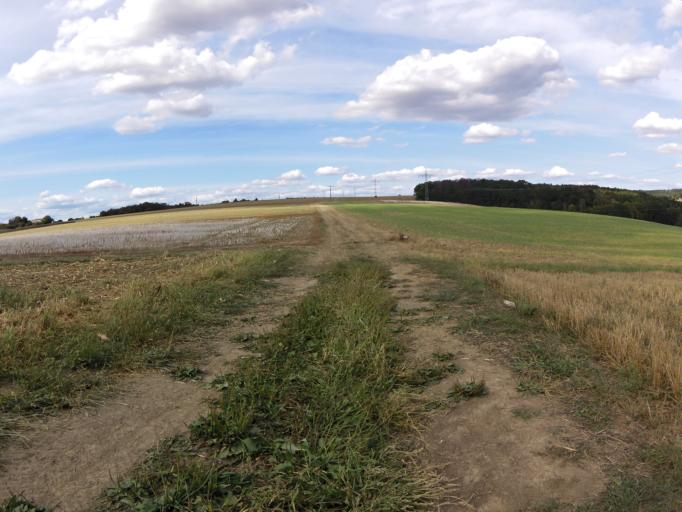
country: DE
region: Bavaria
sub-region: Regierungsbezirk Unterfranken
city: Gadheim
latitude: 49.8560
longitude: 9.9187
